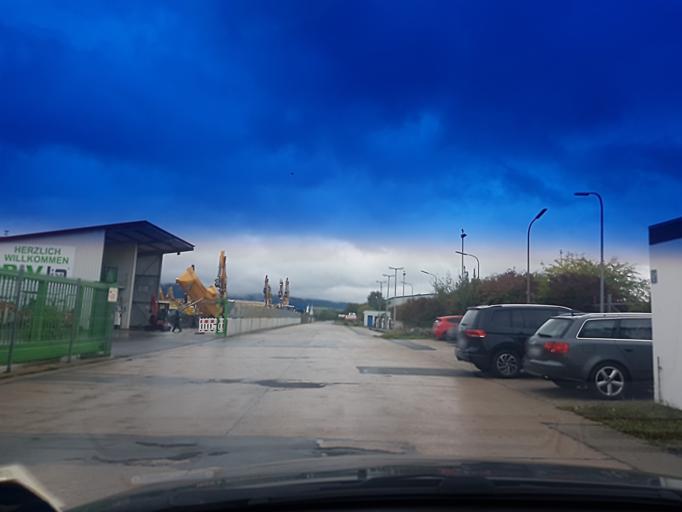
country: DE
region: Bavaria
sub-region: Upper Franconia
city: Bindlach
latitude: 49.9918
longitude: 11.6342
